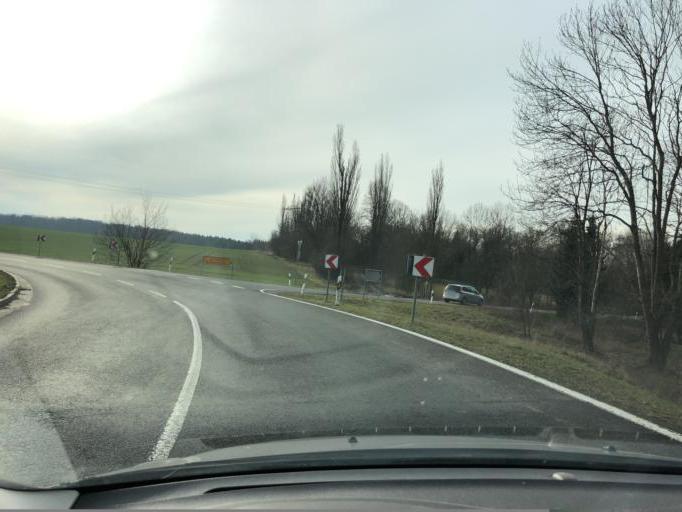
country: DE
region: Thuringia
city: Hardisleben
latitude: 51.1626
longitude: 11.4943
